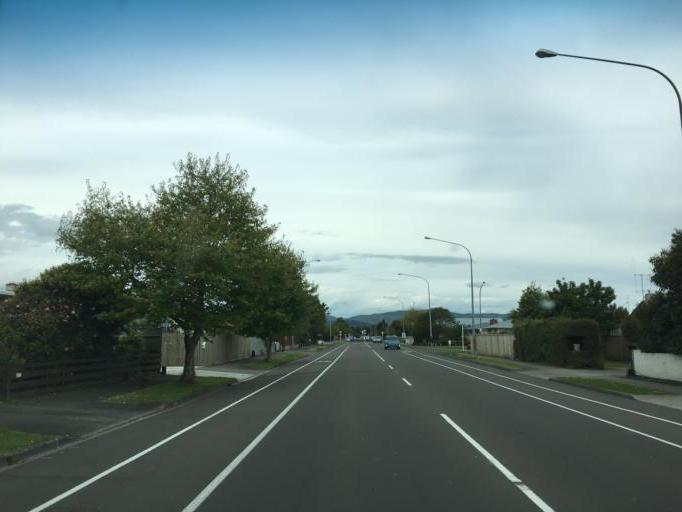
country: NZ
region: Manawatu-Wanganui
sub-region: Palmerston North City
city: Palmerston North
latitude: -40.3656
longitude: 175.5961
